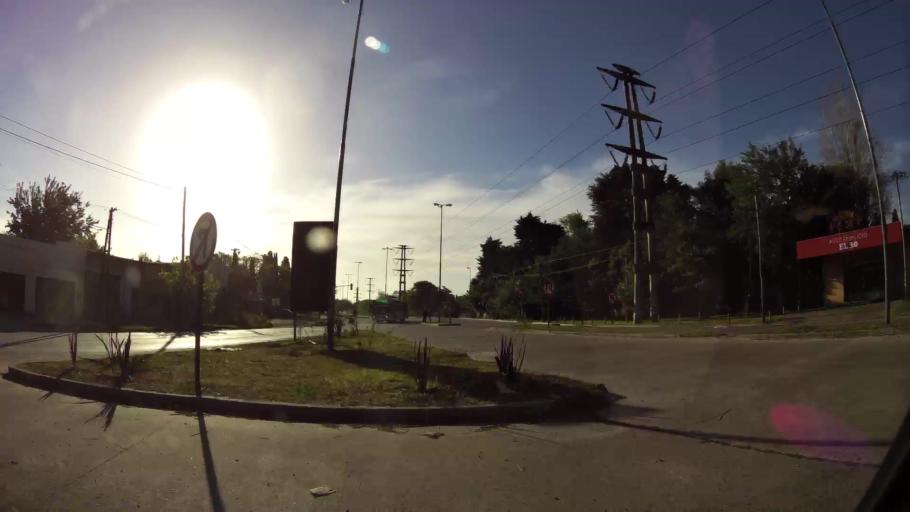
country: AR
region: Buenos Aires
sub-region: Partido de Quilmes
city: Quilmes
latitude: -34.8119
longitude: -58.2058
